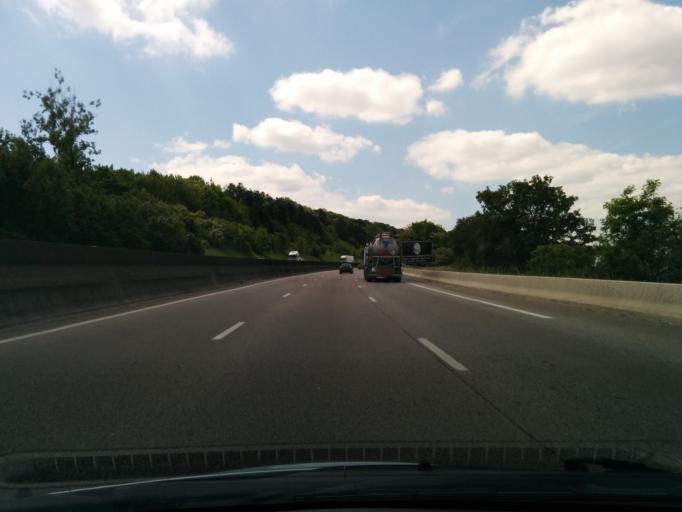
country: FR
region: Ile-de-France
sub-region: Departement des Yvelines
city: Porcheville
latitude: 48.9654
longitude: 1.7529
